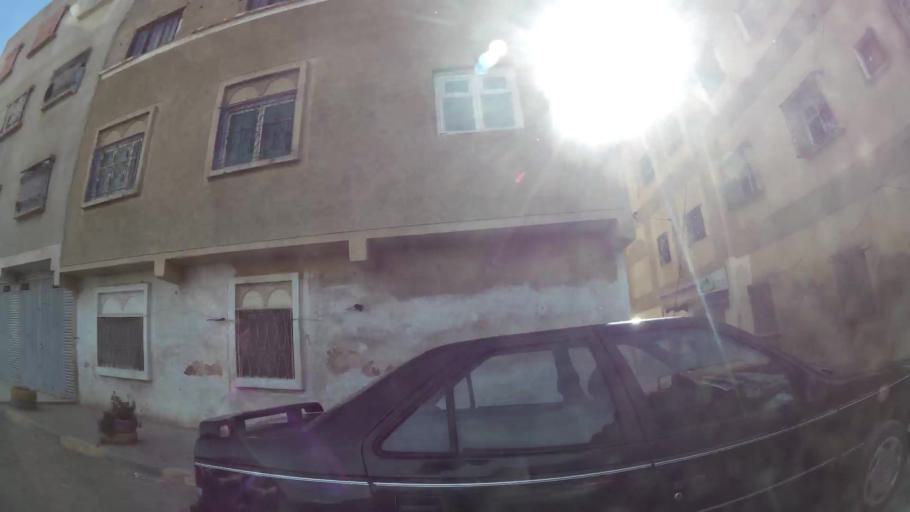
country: MA
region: Fes-Boulemane
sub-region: Fes
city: Fes
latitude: 34.0153
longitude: -5.0322
